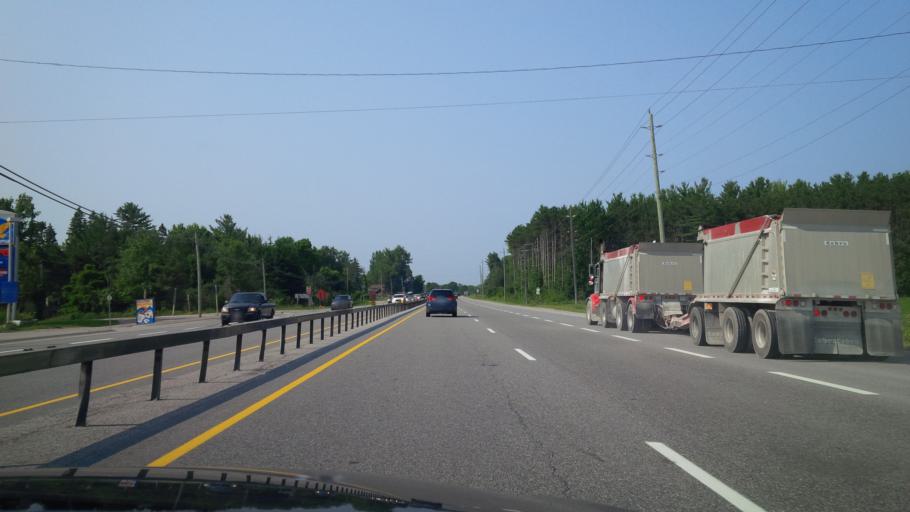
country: CA
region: Ontario
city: Orillia
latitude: 44.7111
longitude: -79.3845
